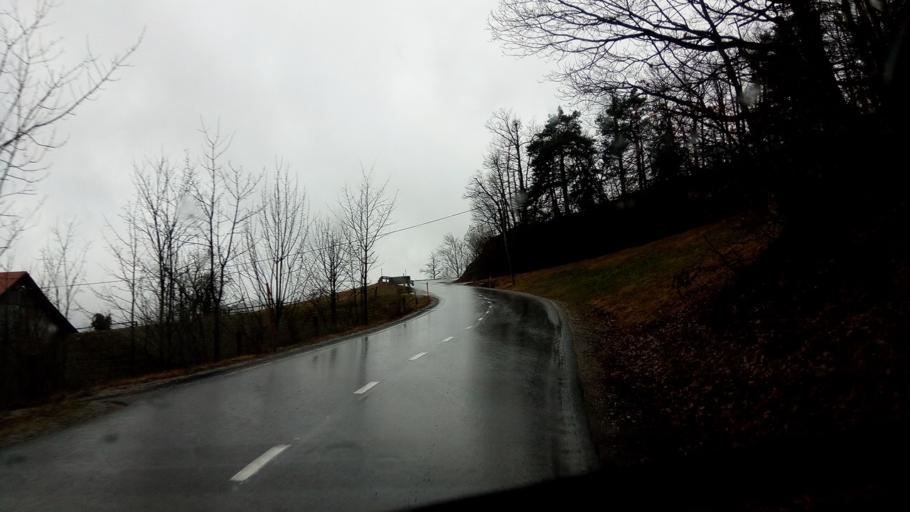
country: SI
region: Horjul
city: Horjul
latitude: 46.0217
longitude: 14.2066
